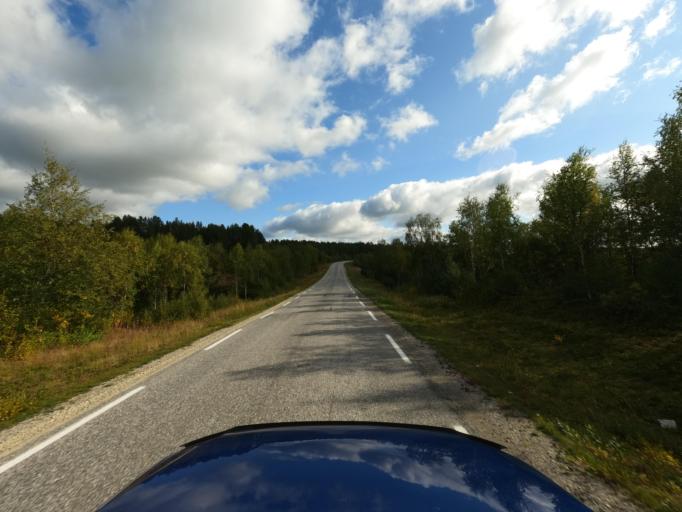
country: NO
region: Finnmark Fylke
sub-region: Karasjok
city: Karasjohka
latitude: 69.4436
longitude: 25.2391
